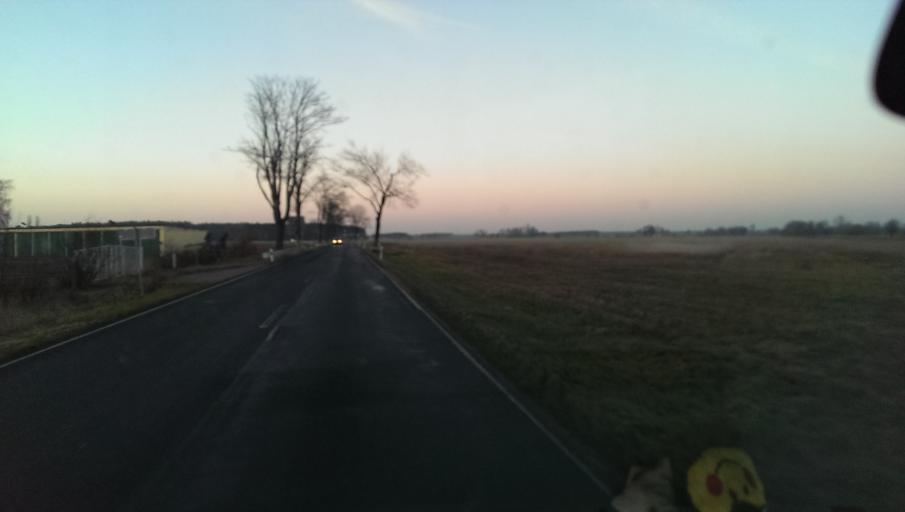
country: DE
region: Saxony-Anhalt
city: Holzdorf
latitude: 51.8000
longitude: 13.1787
